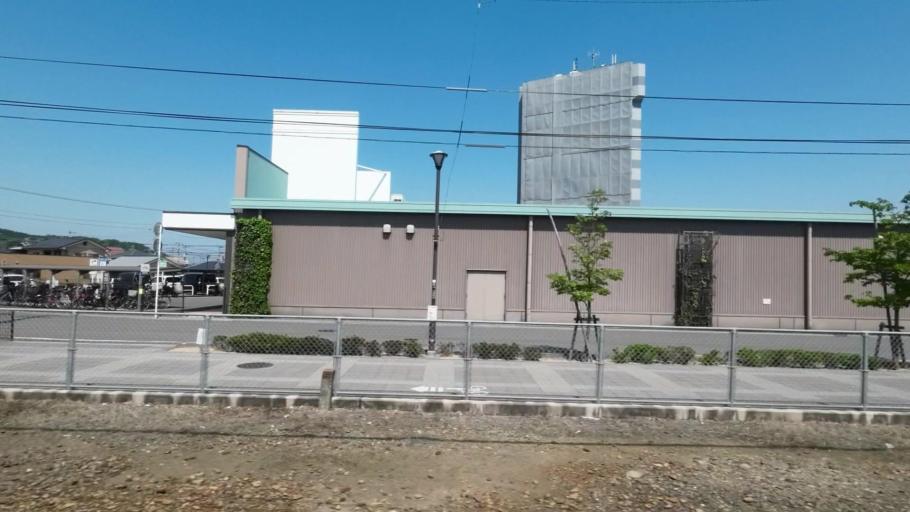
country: JP
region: Ehime
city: Niihama
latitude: 33.9465
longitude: 133.2930
